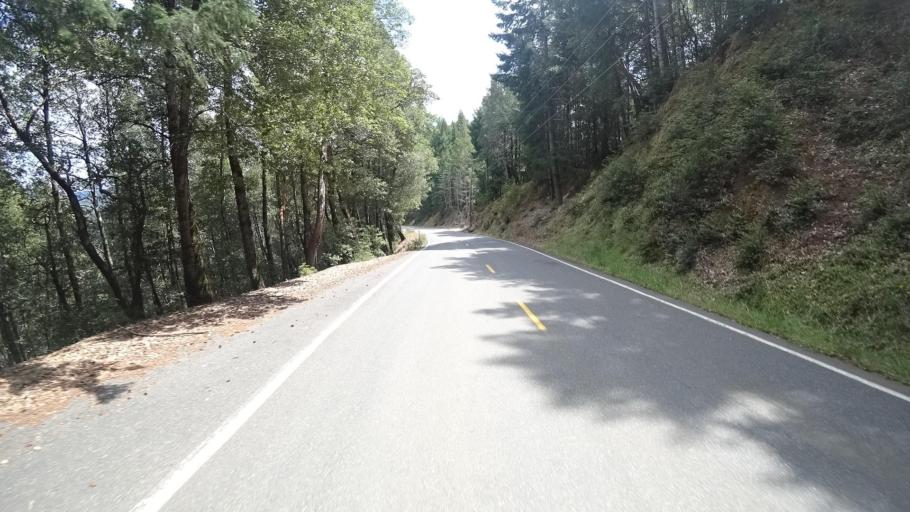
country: US
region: California
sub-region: Humboldt County
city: Redway
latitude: 40.0547
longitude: -123.9902
